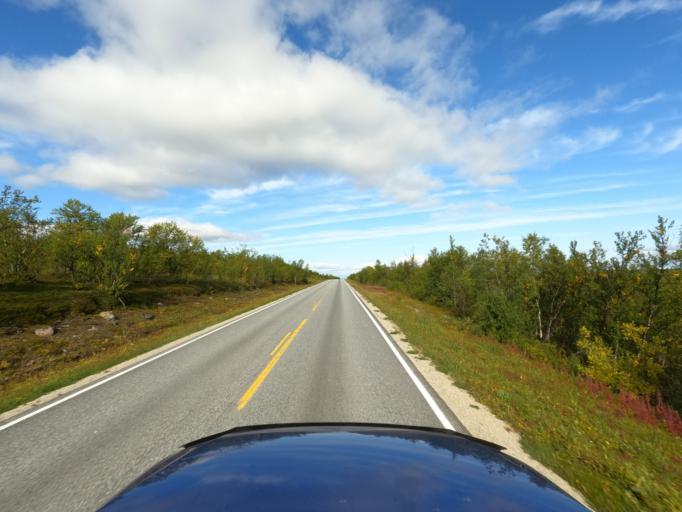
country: NO
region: Finnmark Fylke
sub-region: Karasjok
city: Karasjohka
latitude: 69.6515
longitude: 25.2793
